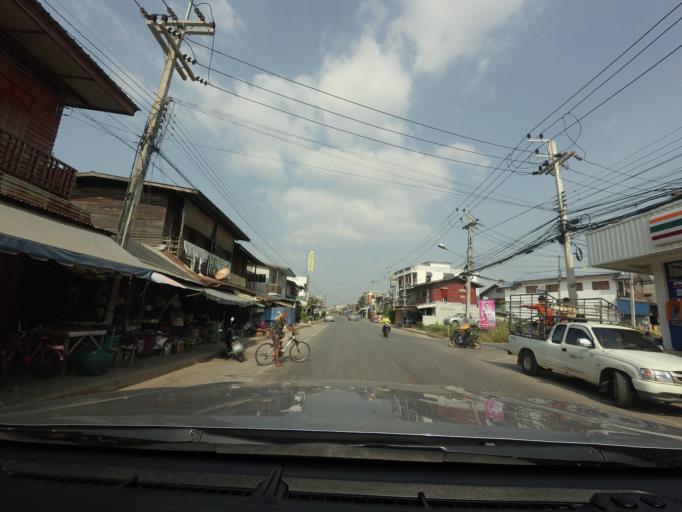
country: TH
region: Sukhothai
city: Kong Krailat
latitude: 16.9446
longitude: 99.9694
